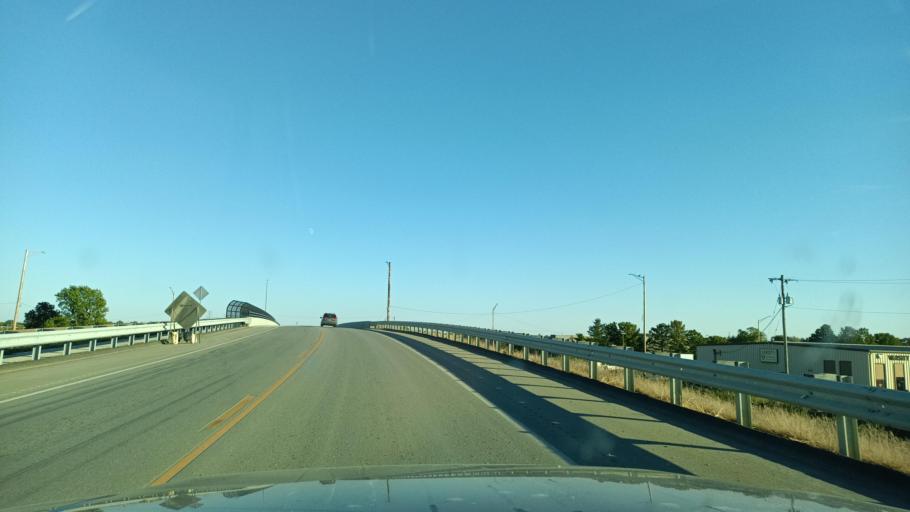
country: US
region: Illinois
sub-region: Champaign County
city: Champaign
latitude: 40.1441
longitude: -88.2882
